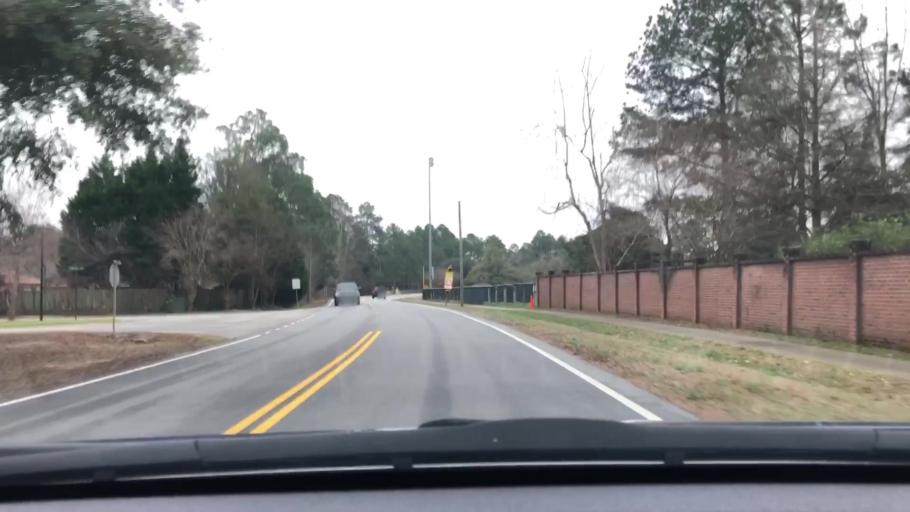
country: US
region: South Carolina
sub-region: Sumter County
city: Cherryvale
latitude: 33.9377
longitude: -80.4047
